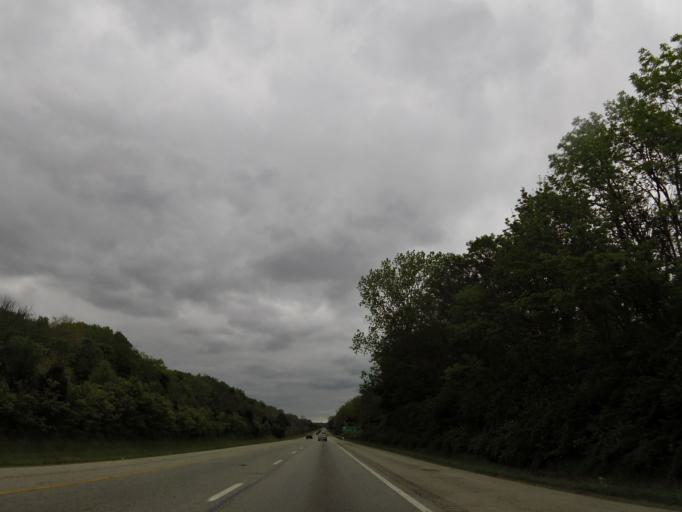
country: US
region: Ohio
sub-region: Warren County
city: South Lebanon
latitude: 39.3885
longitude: -84.2051
